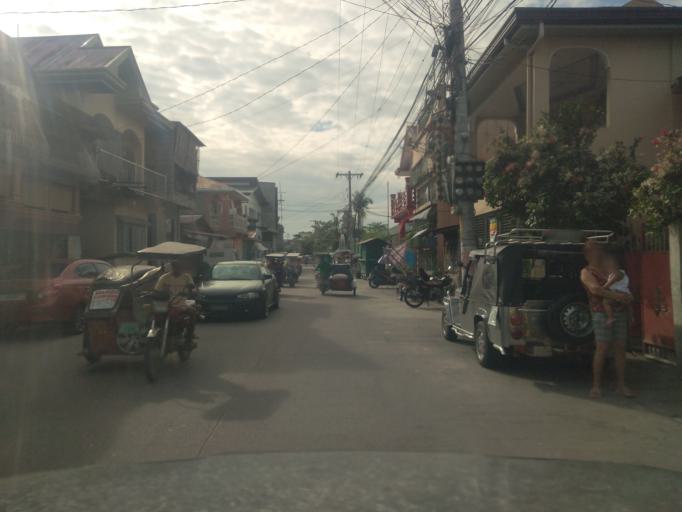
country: PH
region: Central Luzon
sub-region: Province of Pampanga
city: Sexmoan
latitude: 14.9384
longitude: 120.6215
